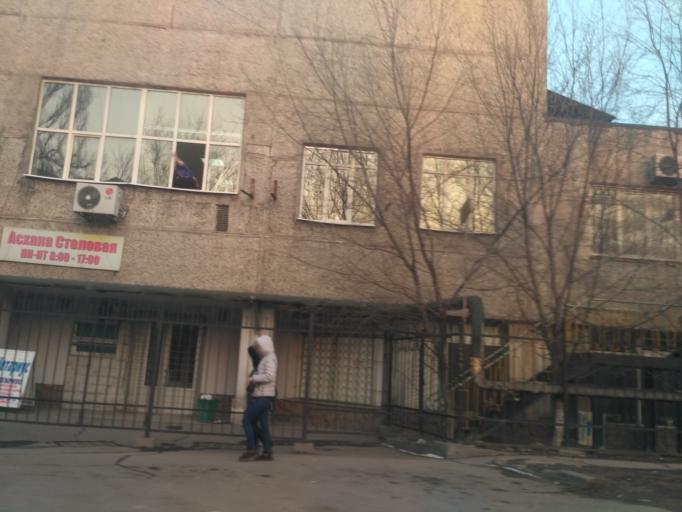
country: KZ
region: Almaty Qalasy
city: Almaty
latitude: 43.2665
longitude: 76.8634
